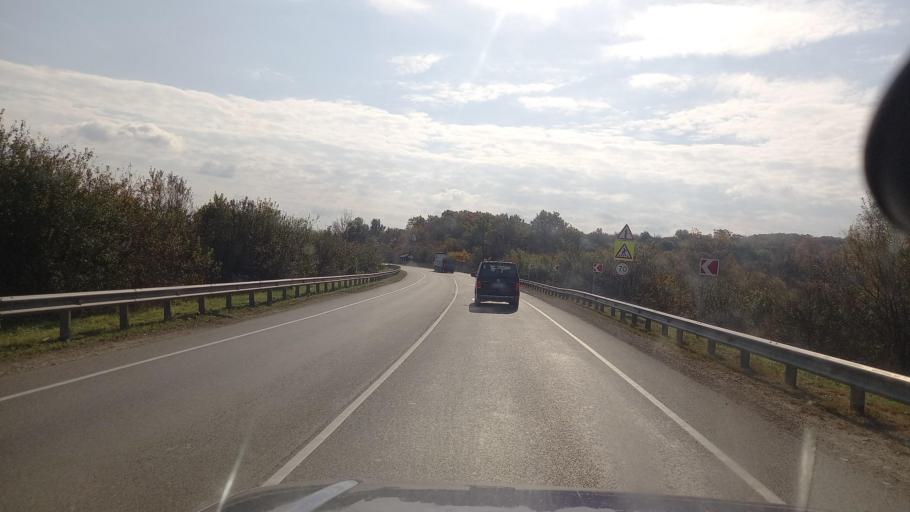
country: RU
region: Krasnodarskiy
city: Abinsk
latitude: 44.8514
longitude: 38.1350
